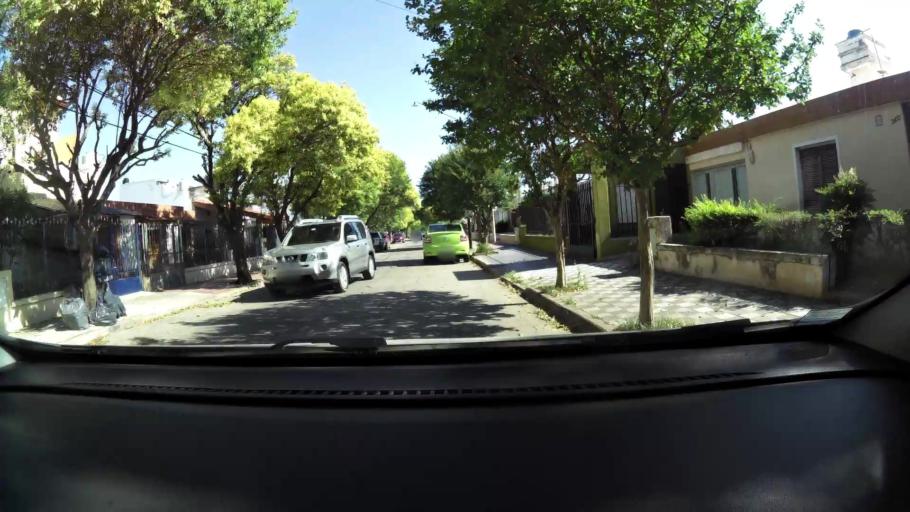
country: AR
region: Cordoba
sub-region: Departamento de Capital
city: Cordoba
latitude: -31.3740
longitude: -64.1818
